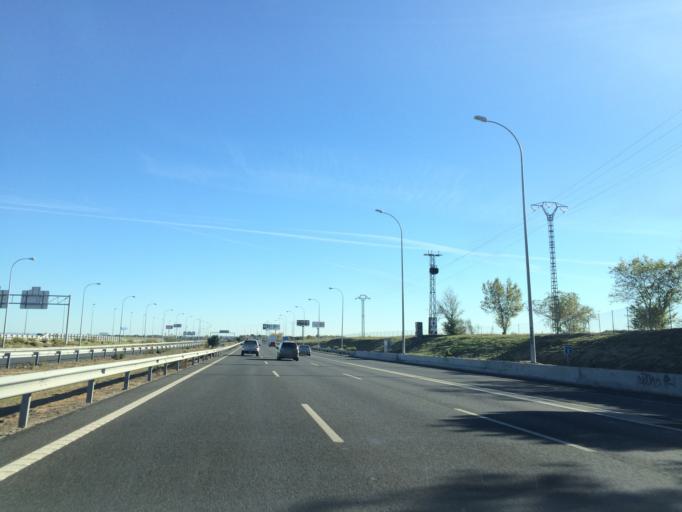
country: ES
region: Madrid
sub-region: Provincia de Madrid
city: Alcorcon
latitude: 40.3907
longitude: -3.8303
